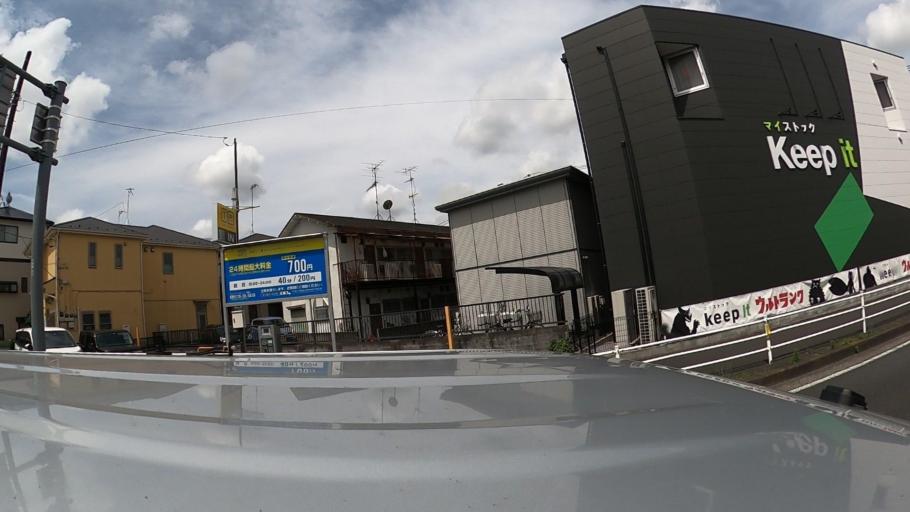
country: JP
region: Kanagawa
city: Minami-rinkan
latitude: 35.4151
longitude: 139.4697
